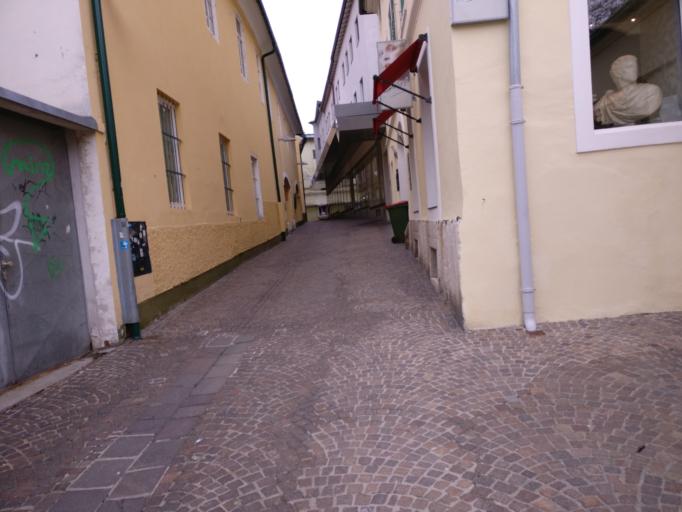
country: AT
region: Carinthia
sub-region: Villach Stadt
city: Villach
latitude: 46.6143
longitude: 13.8453
